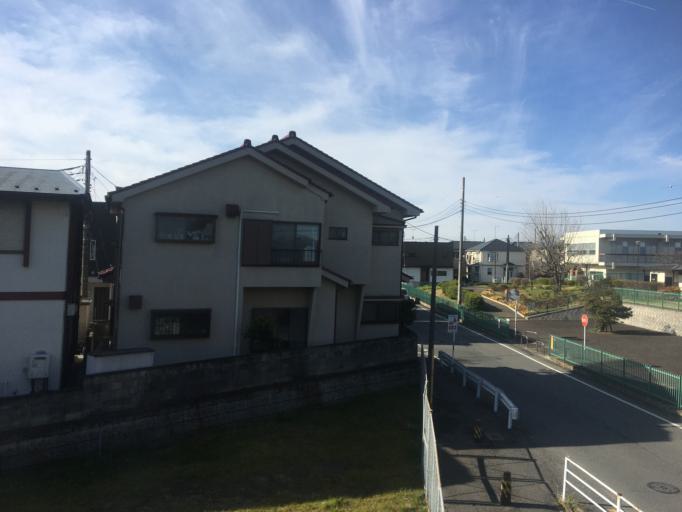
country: JP
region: Saitama
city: Kawagoe
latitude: 35.9294
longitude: 139.4359
